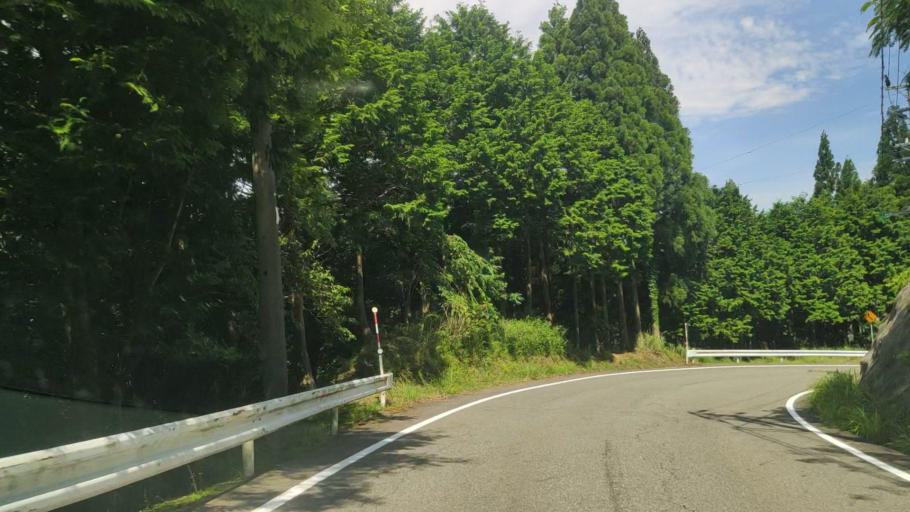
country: JP
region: Hyogo
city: Toyooka
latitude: 35.6397
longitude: 134.7668
